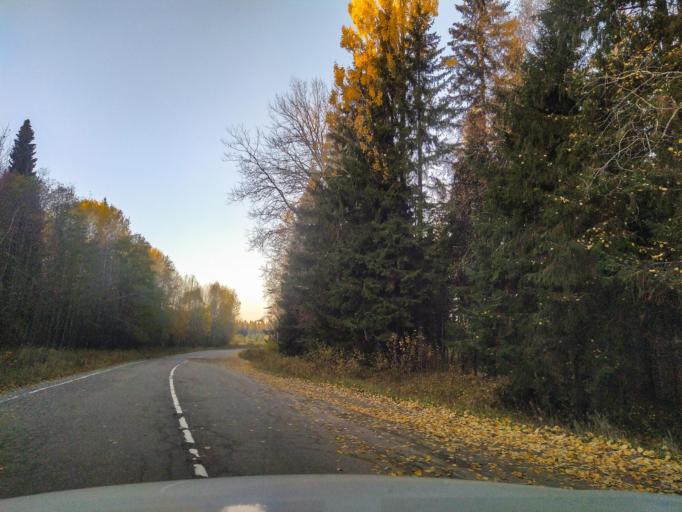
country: RU
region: Leningrad
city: Kuznechnoye
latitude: 61.3447
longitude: 29.9816
